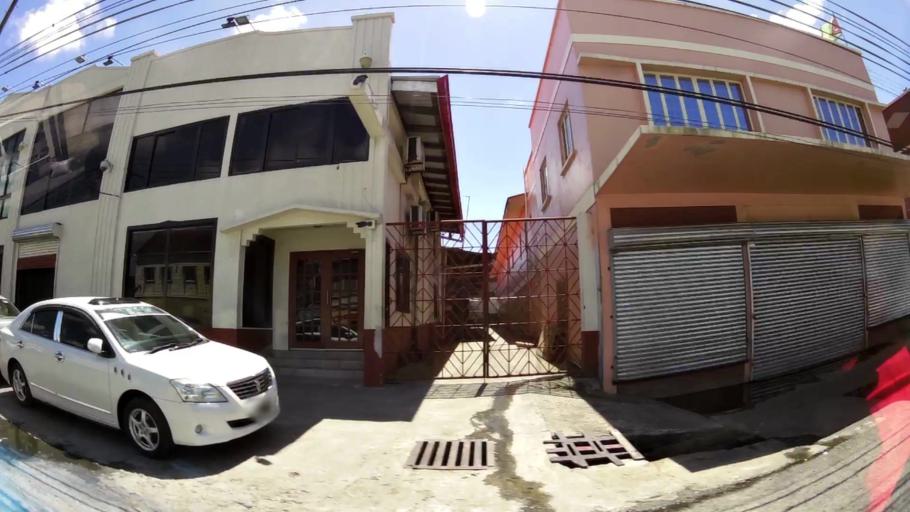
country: GY
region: Demerara-Mahaica
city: Georgetown
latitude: 6.8019
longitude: -58.1675
